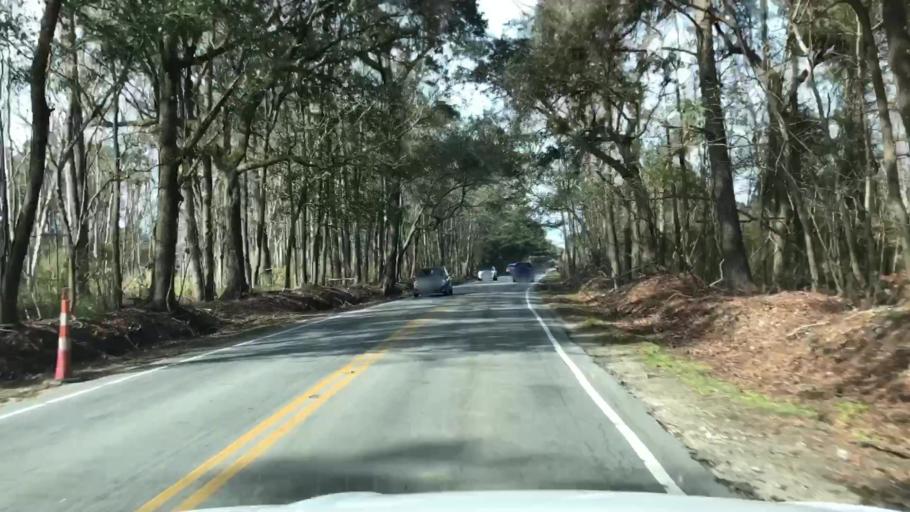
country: US
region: South Carolina
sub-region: Charleston County
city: Shell Point
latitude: 32.7572
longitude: -80.0527
